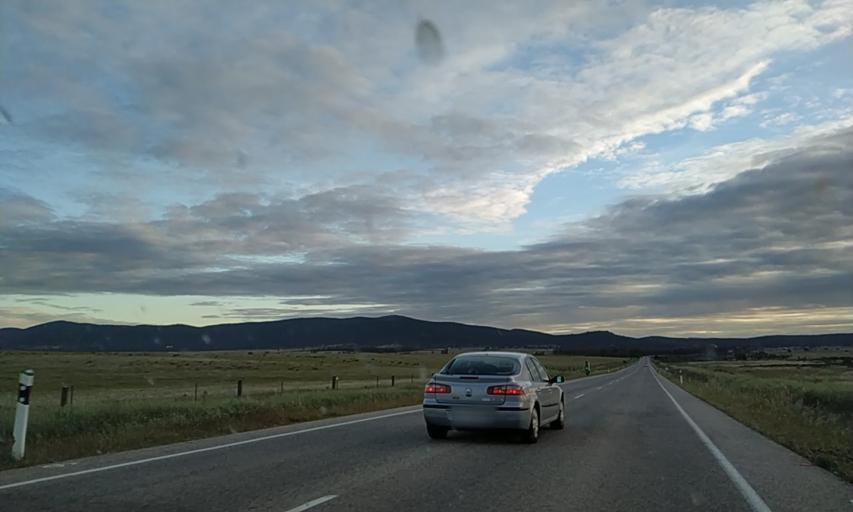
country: ES
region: Extremadura
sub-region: Provincia de Caceres
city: Malpartida de Caceres
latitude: 39.3426
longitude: -6.4758
